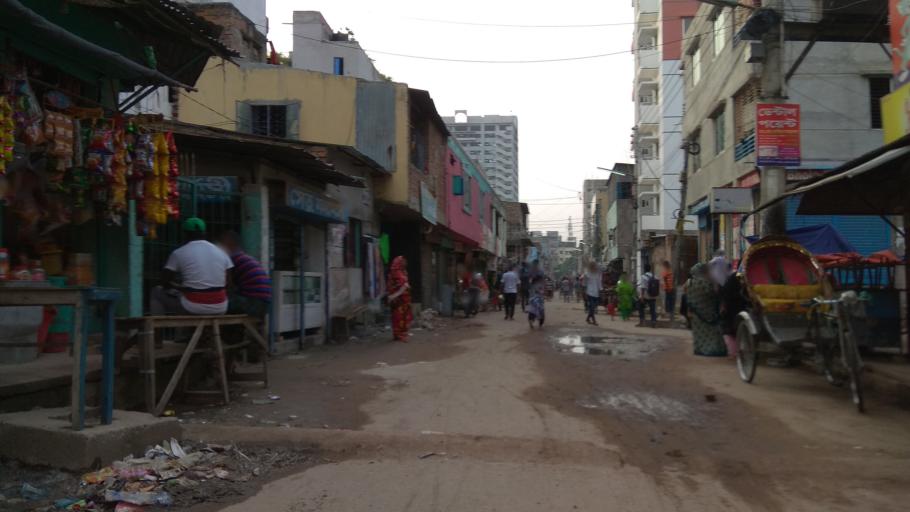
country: BD
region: Dhaka
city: Tungi
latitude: 23.8192
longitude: 90.3759
